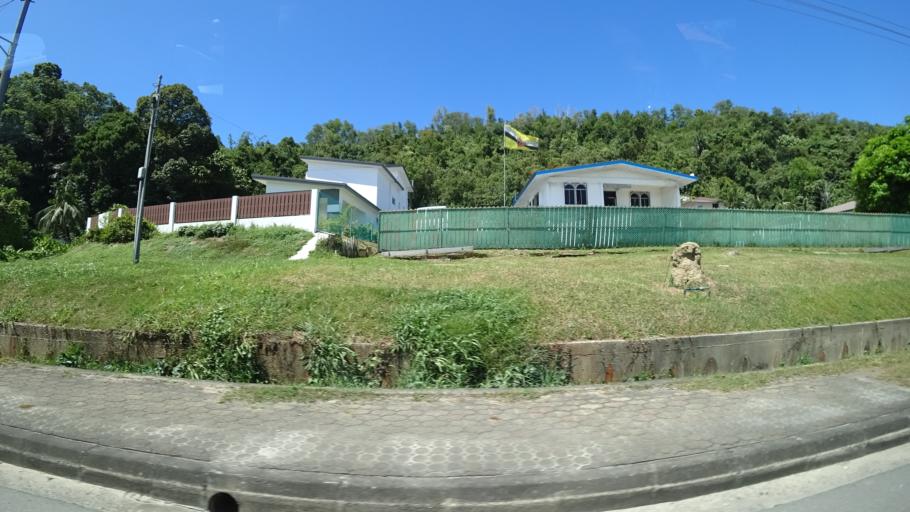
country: BN
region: Brunei and Muara
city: Bandar Seri Begawan
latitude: 4.8524
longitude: 114.8771
